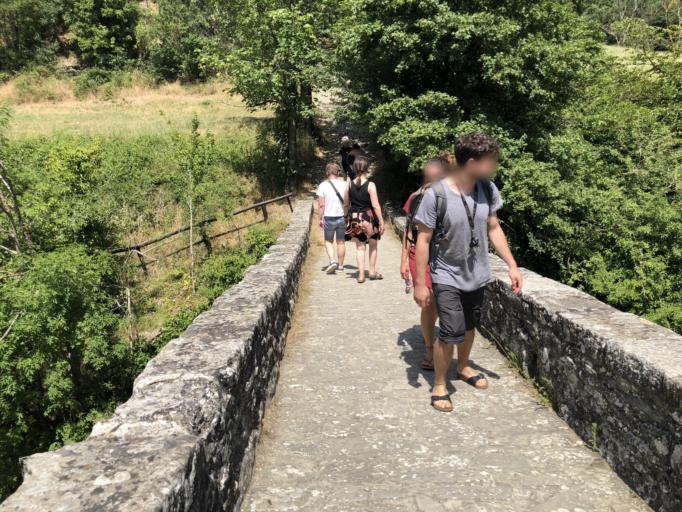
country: IT
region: Emilia-Romagna
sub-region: Forli-Cesena
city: Portico di Romagna
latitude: 44.0072
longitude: 11.7466
